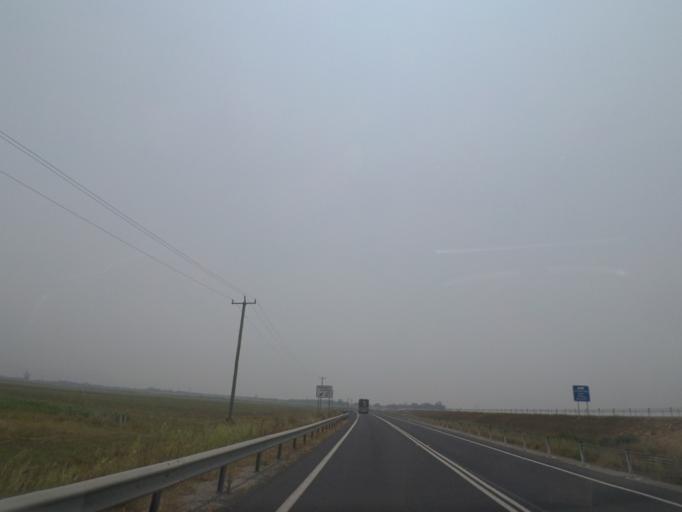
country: AU
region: New South Wales
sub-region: Clarence Valley
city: Maclean
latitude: -29.4119
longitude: 153.2415
